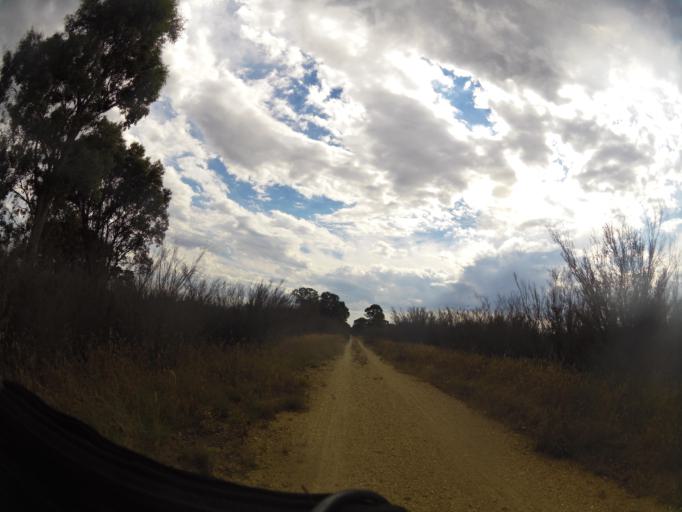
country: AU
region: Victoria
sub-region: Wellington
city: Heyfield
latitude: -38.0420
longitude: 146.6444
